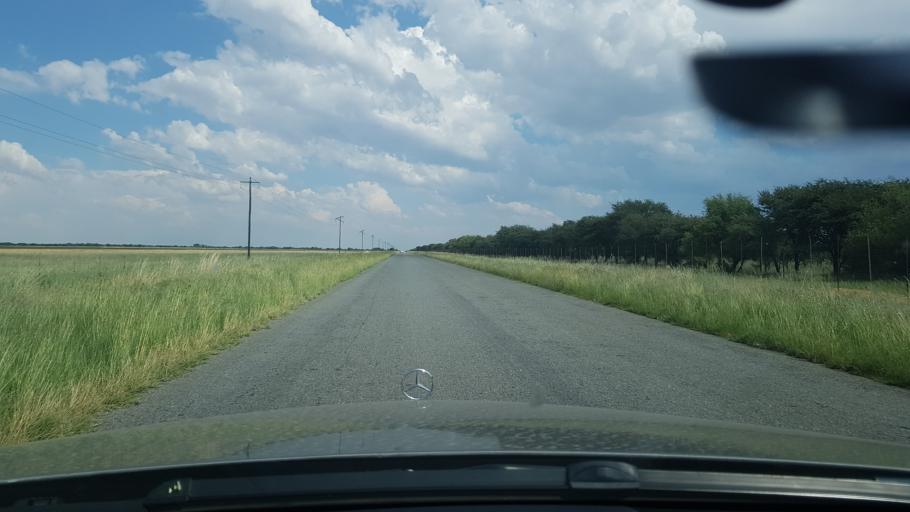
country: ZA
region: North-West
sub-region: Dr Ruth Segomotsi Mompati District Municipality
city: Bloemhof
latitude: -27.7434
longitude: 25.5885
